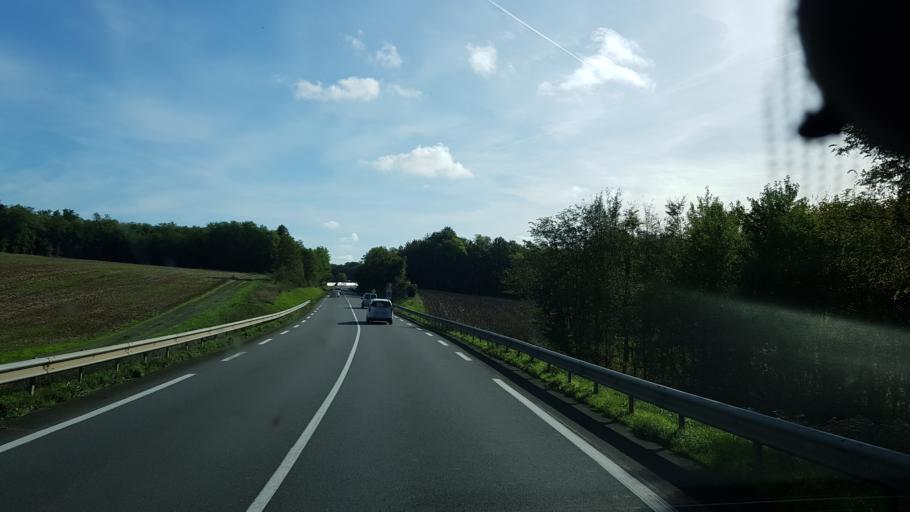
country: FR
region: Poitou-Charentes
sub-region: Departement de la Charente
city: Saint-Claud
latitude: 45.8666
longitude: 0.4657
